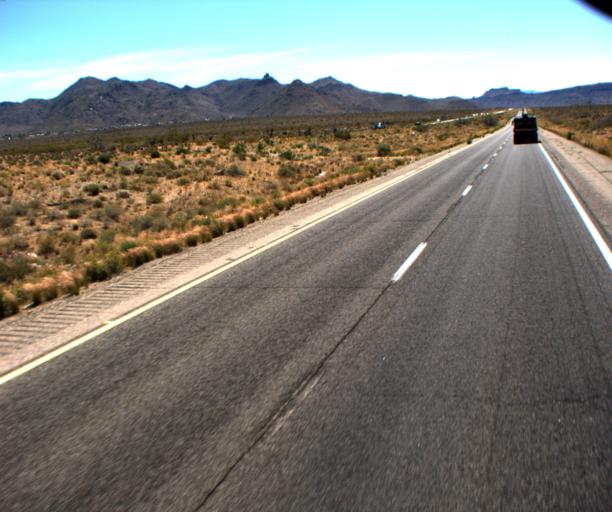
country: US
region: Arizona
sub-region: Mohave County
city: Golden Valley
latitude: 35.2673
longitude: -114.1657
